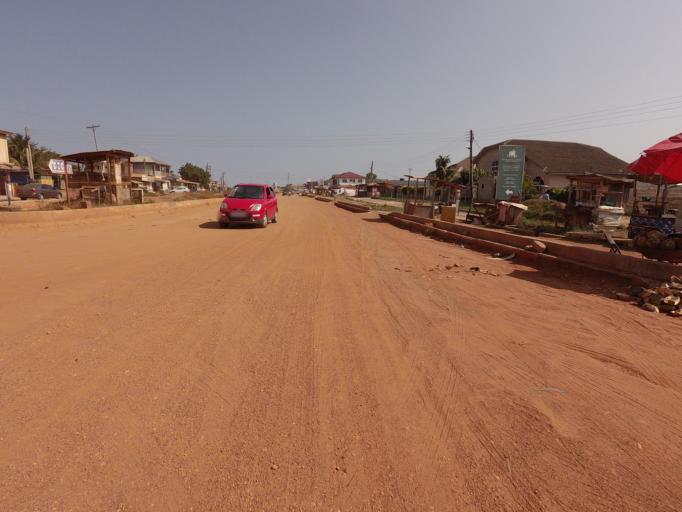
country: GH
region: Greater Accra
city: Teshi Old Town
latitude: 5.6186
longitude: -0.1248
